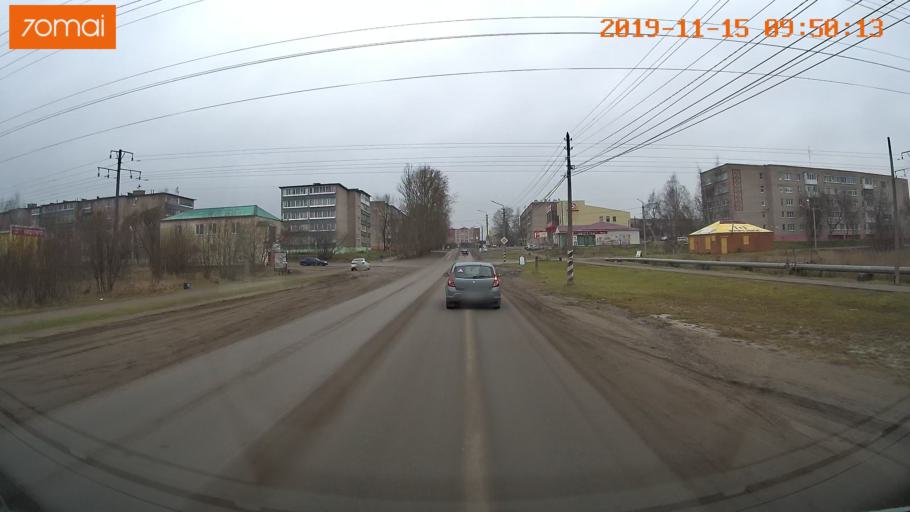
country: RU
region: Vologda
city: Sheksna
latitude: 59.2317
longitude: 38.5129
